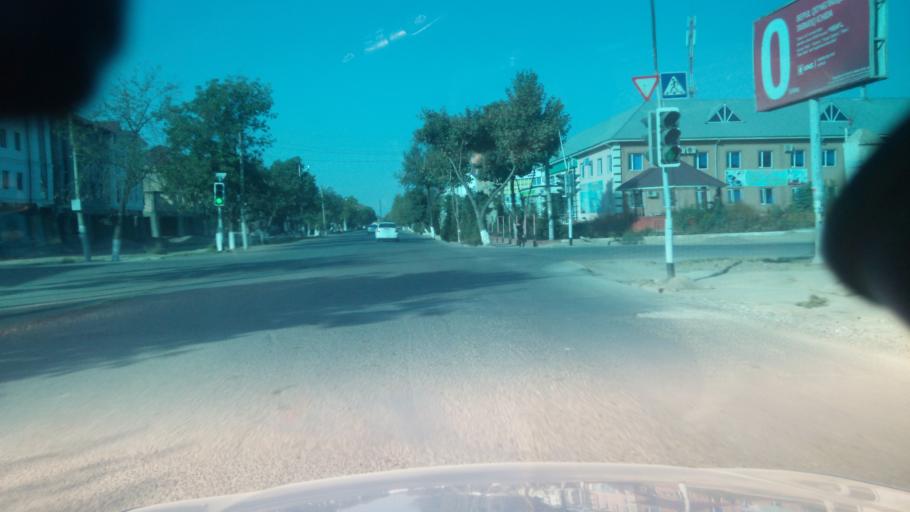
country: UZ
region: Sirdaryo
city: Guliston
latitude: 40.4984
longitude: 68.7708
